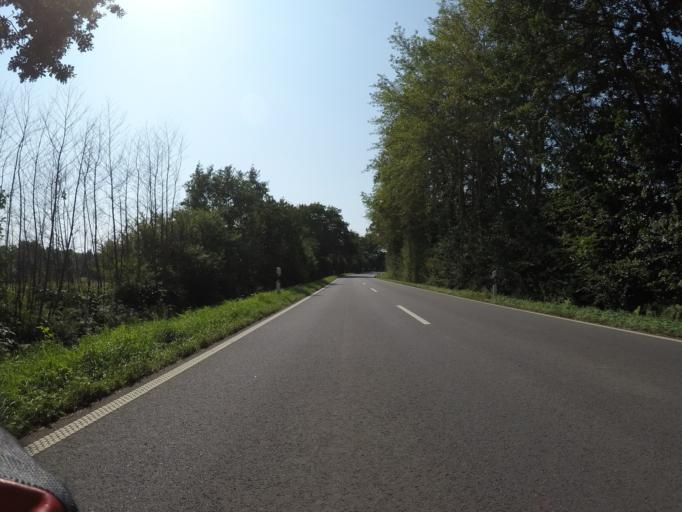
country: DE
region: Schleswig-Holstein
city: Huttblek
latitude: 53.8414
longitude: 10.0565
